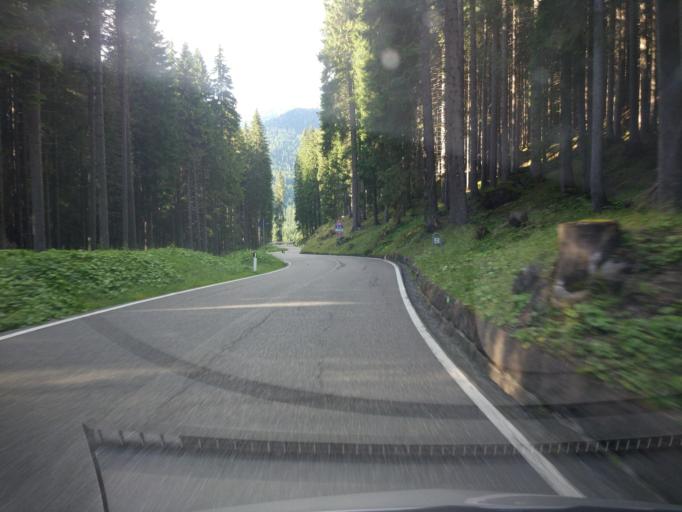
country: IT
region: Veneto
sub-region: Provincia di Belluno
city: Falcade Alto
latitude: 46.3028
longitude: 11.7577
